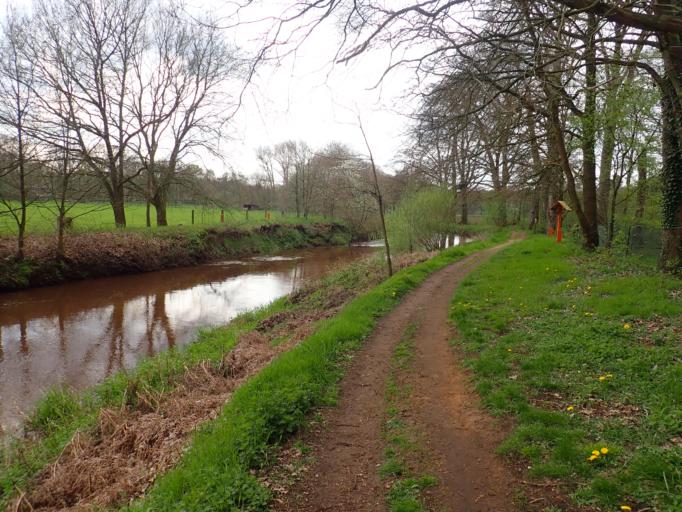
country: BE
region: Flanders
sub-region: Provincie Antwerpen
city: Herentals
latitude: 51.1869
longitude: 4.8071
